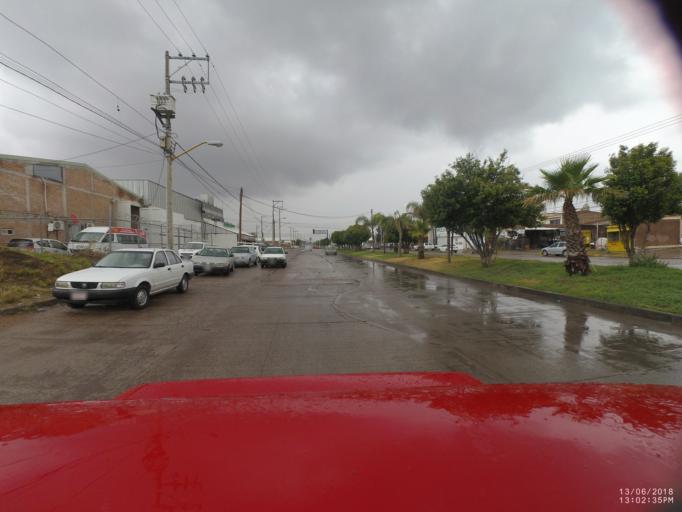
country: MX
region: Aguascalientes
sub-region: Jesus Maria
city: Arboledas Paso Blanco [Fraccionamiento]
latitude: 21.9680
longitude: -102.2931
